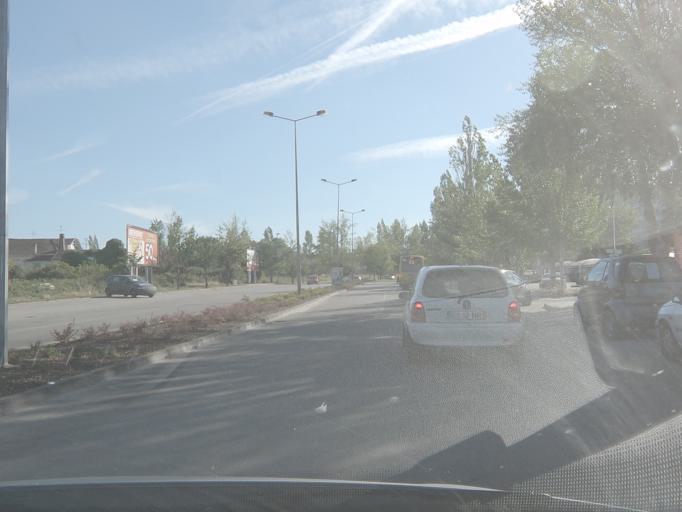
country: PT
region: Viseu
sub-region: Viseu
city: Abraveses
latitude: 40.6721
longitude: -7.9177
